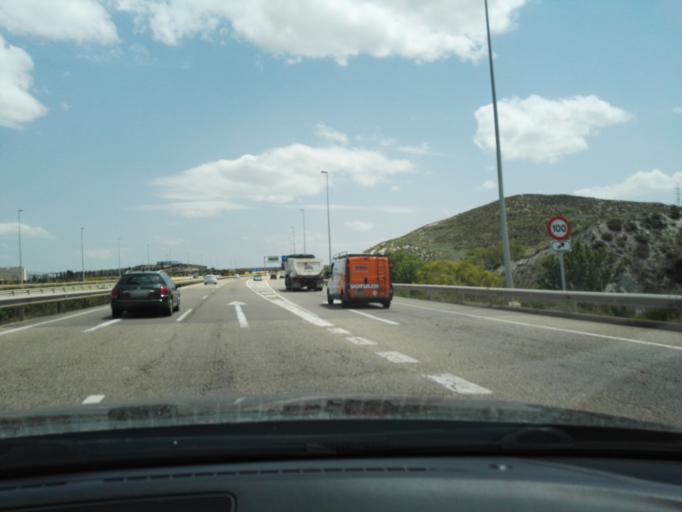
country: ES
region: Aragon
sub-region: Provincia de Zaragoza
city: Montecanal
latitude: 41.6174
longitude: -0.9389
